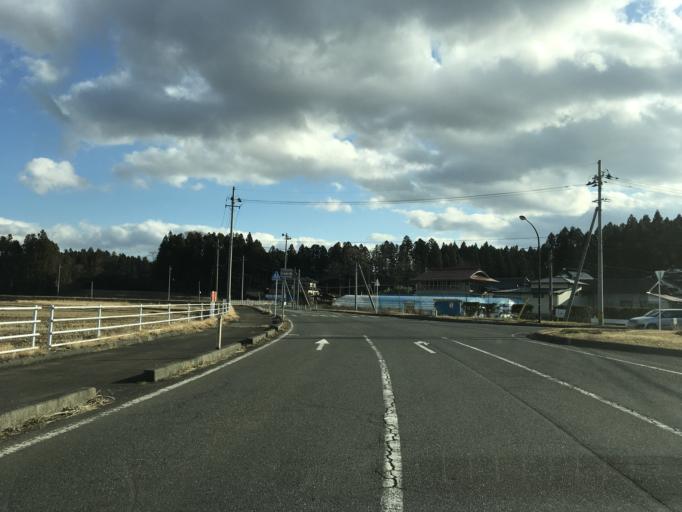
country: JP
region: Iwate
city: Ichinoseki
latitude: 38.8211
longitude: 141.0027
